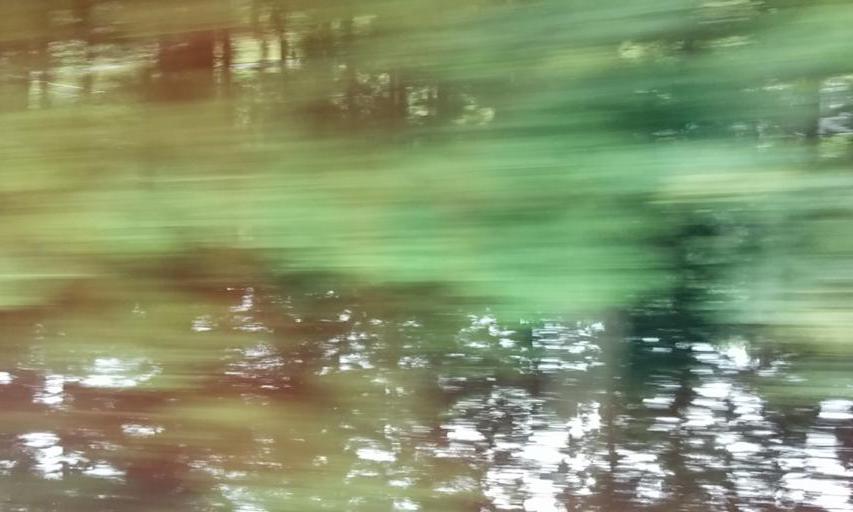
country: JP
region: Tochigi
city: Imaichi
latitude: 36.6929
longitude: 139.7109
